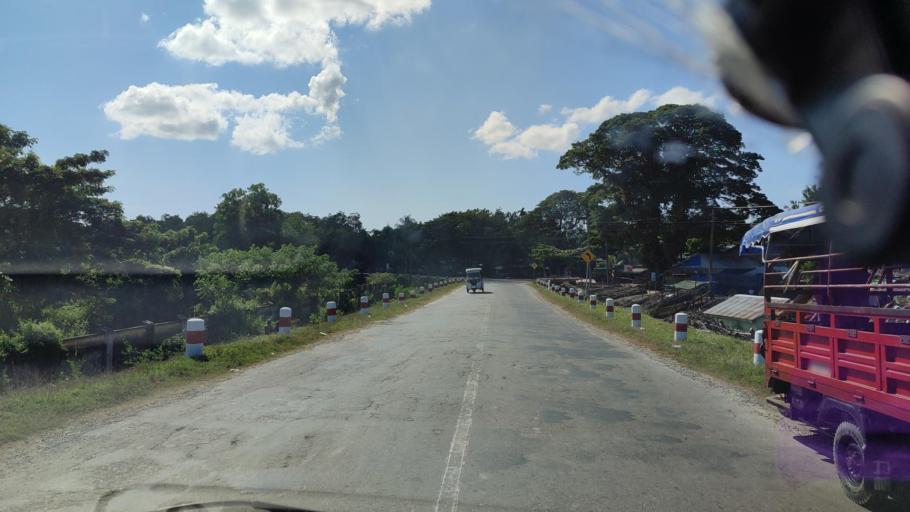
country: MM
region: Rakhine
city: Sittwe
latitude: 20.2211
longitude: 92.8545
